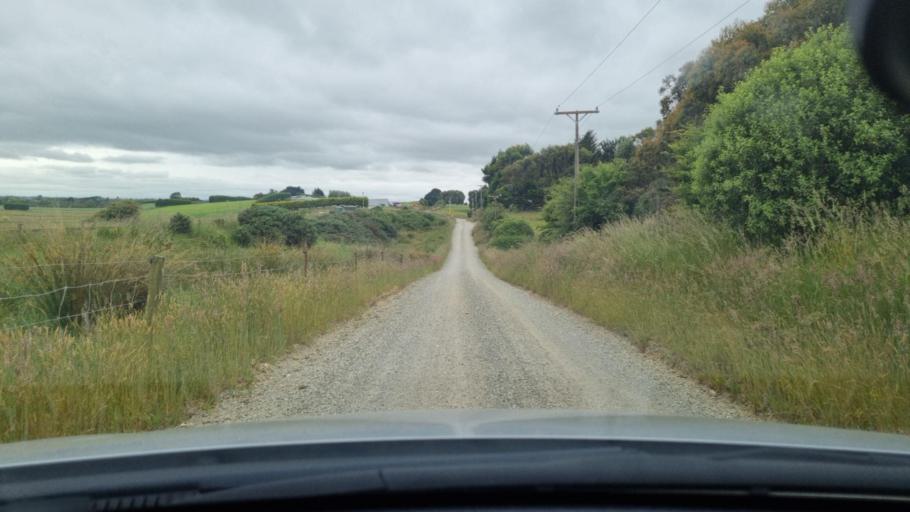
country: NZ
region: Southland
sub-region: Invercargill City
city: Invercargill
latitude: -46.3252
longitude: 168.3405
